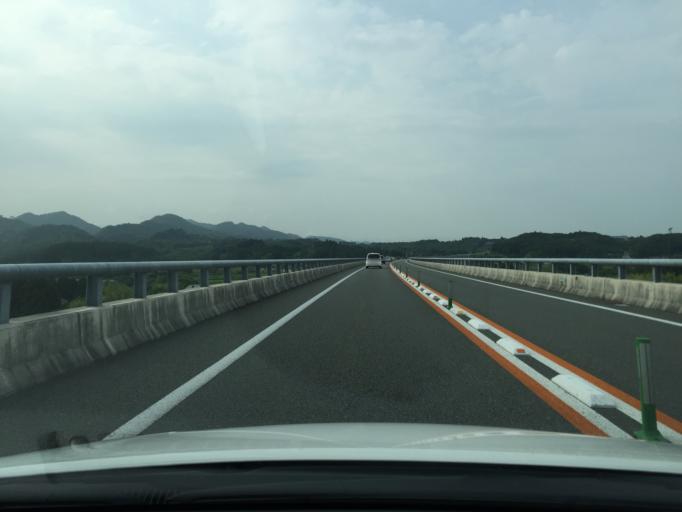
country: JP
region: Fukushima
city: Namie
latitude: 37.2739
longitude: 140.9830
